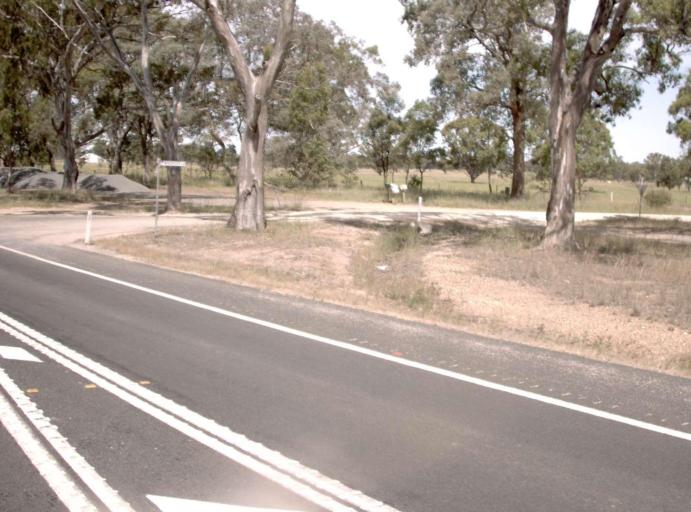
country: AU
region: Victoria
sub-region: Wellington
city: Sale
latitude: -37.9261
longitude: 147.2224
